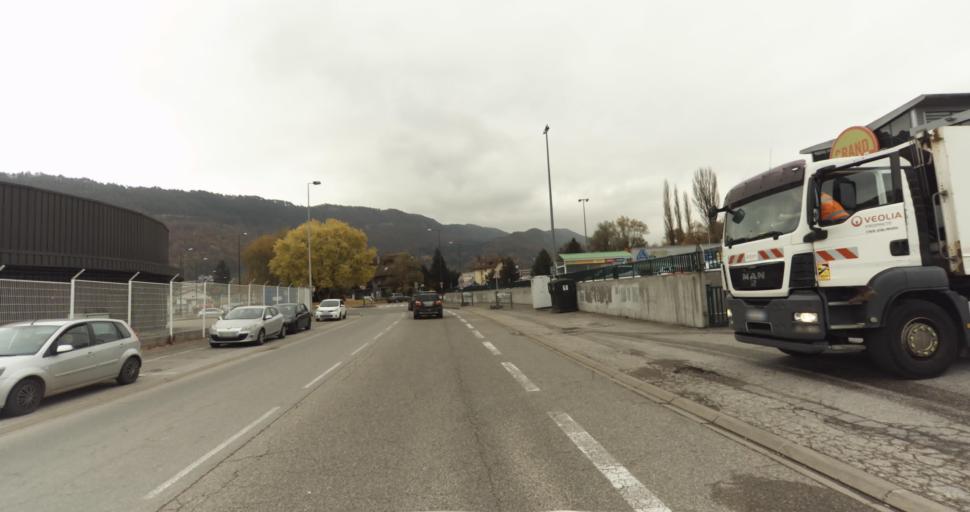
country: FR
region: Rhone-Alpes
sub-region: Departement de la Haute-Savoie
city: Annecy
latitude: 45.8907
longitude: 6.1142
